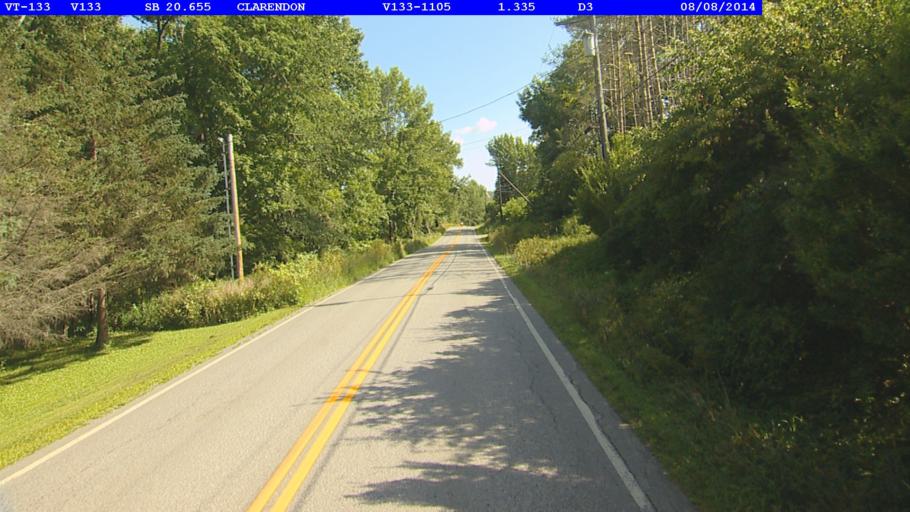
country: US
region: Vermont
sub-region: Rutland County
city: West Rutland
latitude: 43.5694
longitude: -73.0334
